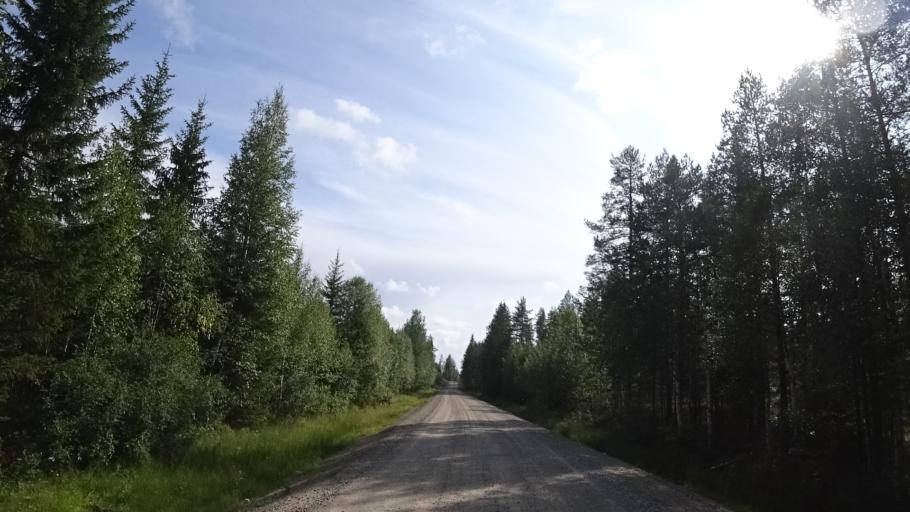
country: FI
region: North Karelia
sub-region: Pielisen Karjala
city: Lieksa
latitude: 63.5912
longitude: 30.1357
